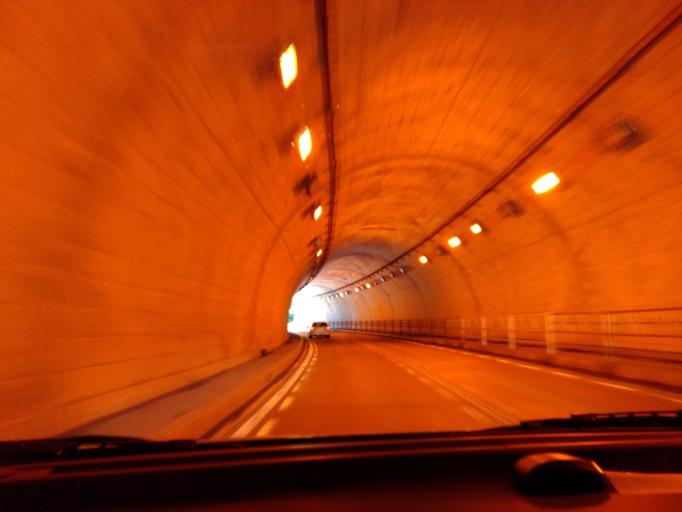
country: JP
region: Akita
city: Yokotemachi
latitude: 39.2507
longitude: 140.5631
